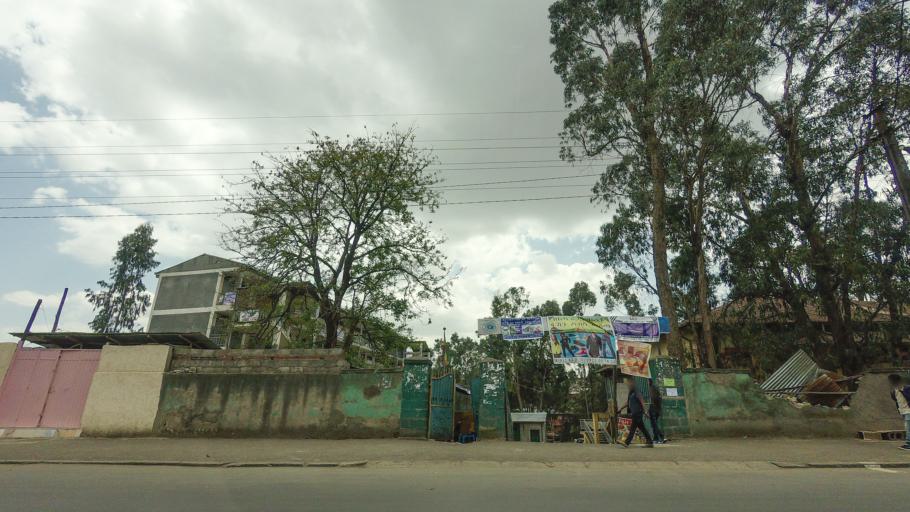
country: ET
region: Adis Abeba
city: Addis Ababa
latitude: 9.0374
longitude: 38.7573
